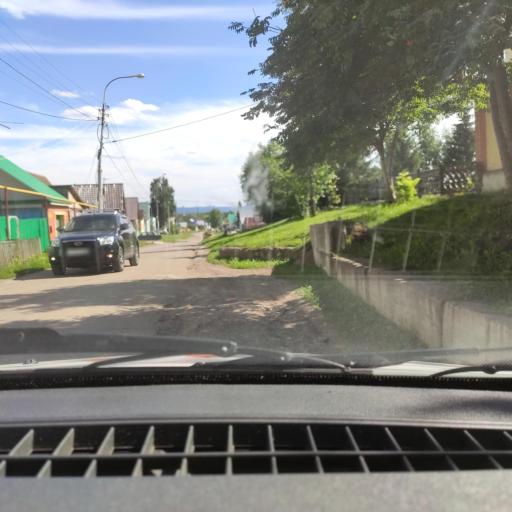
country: RU
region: Bashkortostan
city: Blagoveshchensk
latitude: 55.0468
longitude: 55.9610
